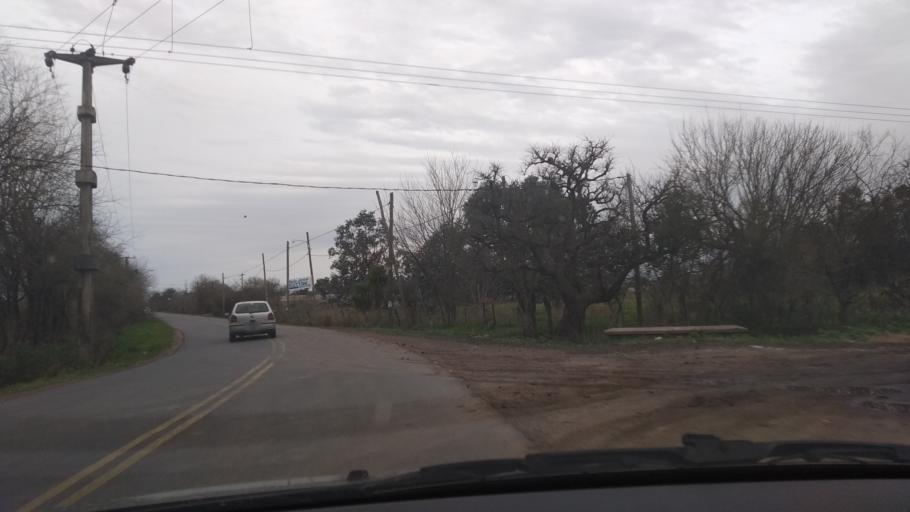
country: AR
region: Buenos Aires
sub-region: Partido de La Plata
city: La Plata
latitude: -35.0008
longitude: -58.0667
